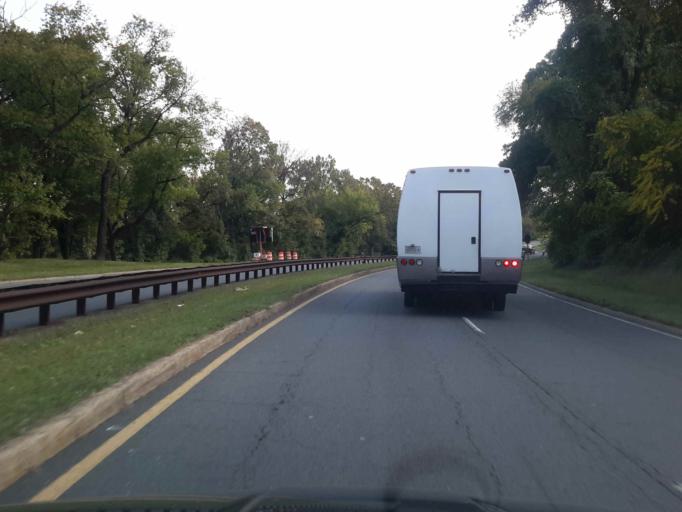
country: US
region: Virginia
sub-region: City of Alexandria
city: Alexandria
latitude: 38.8384
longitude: -77.0462
